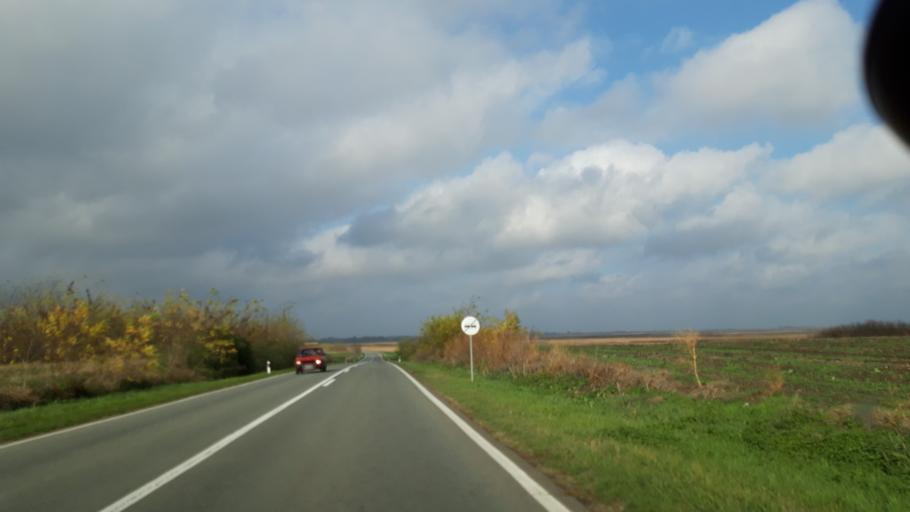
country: RS
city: Ostojicevo
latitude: 45.9031
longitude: 20.1549
